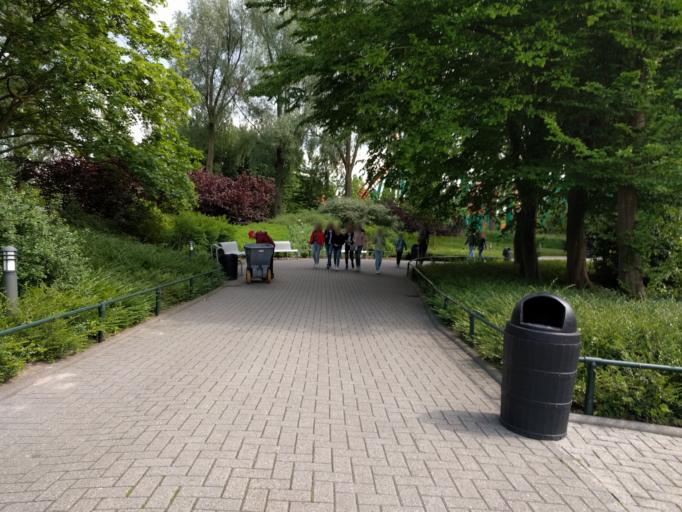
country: NL
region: Gelderland
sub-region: Gemeente Nunspeet
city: Nunspeet
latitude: 52.4414
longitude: 5.7607
